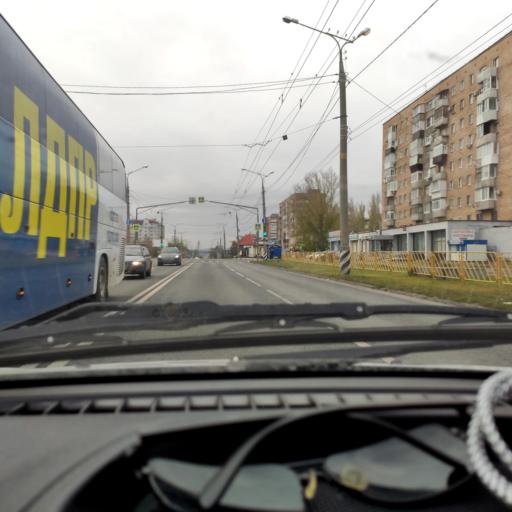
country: RU
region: Samara
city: Zhigulevsk
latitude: 53.4852
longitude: 49.4864
